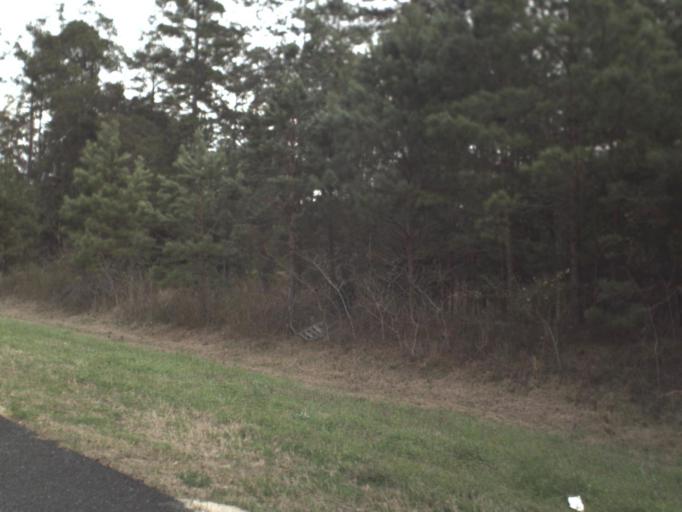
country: US
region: Florida
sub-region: Leon County
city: Tallahassee
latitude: 30.5768
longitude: -84.2019
